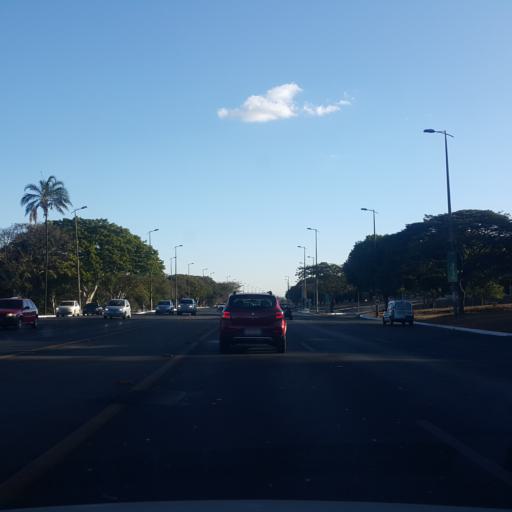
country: BR
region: Federal District
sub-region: Brasilia
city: Brasilia
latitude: -15.8121
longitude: -47.8950
